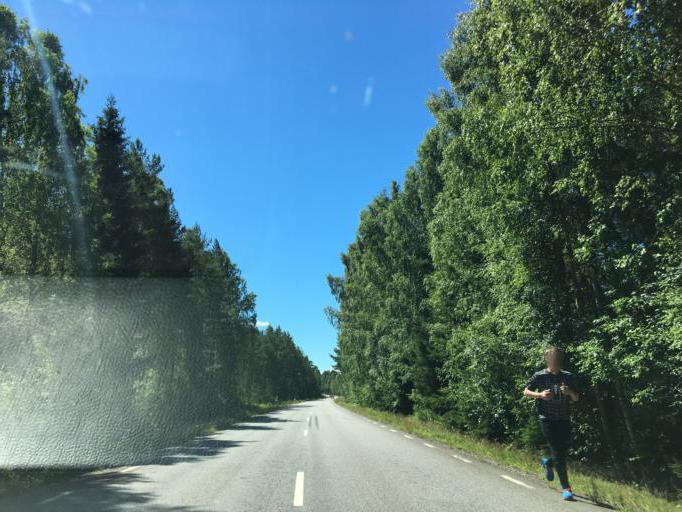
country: SE
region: OErebro
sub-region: Laxa Kommun
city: Laxa
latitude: 58.7883
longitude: 14.5397
